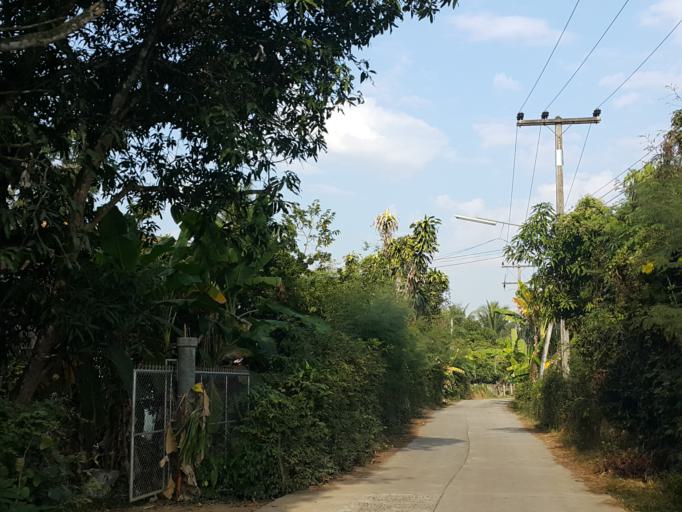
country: TH
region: Chiang Mai
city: San Sai
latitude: 18.8264
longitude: 99.1191
